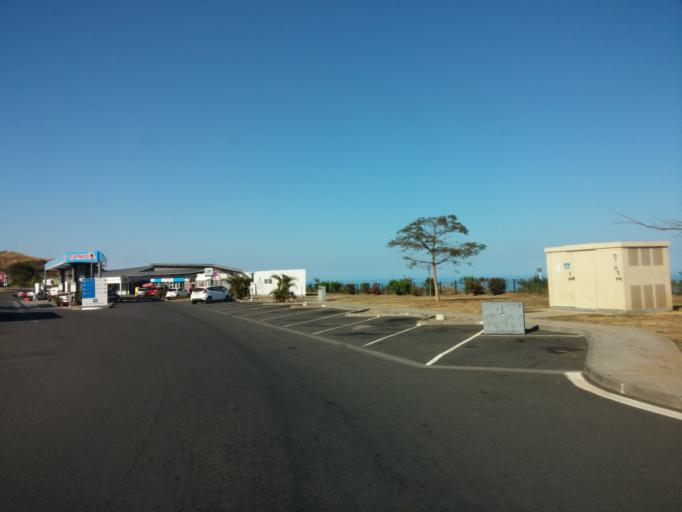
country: RE
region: Reunion
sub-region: Reunion
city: Trois-Bassins
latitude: -21.0876
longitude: 55.2555
